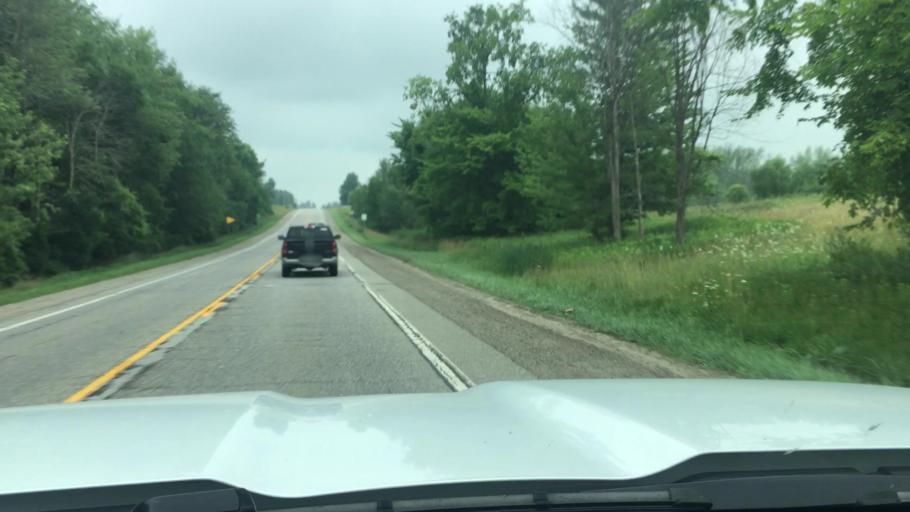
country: US
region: Michigan
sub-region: Sanilac County
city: Marlette
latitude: 43.2492
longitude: -83.0792
